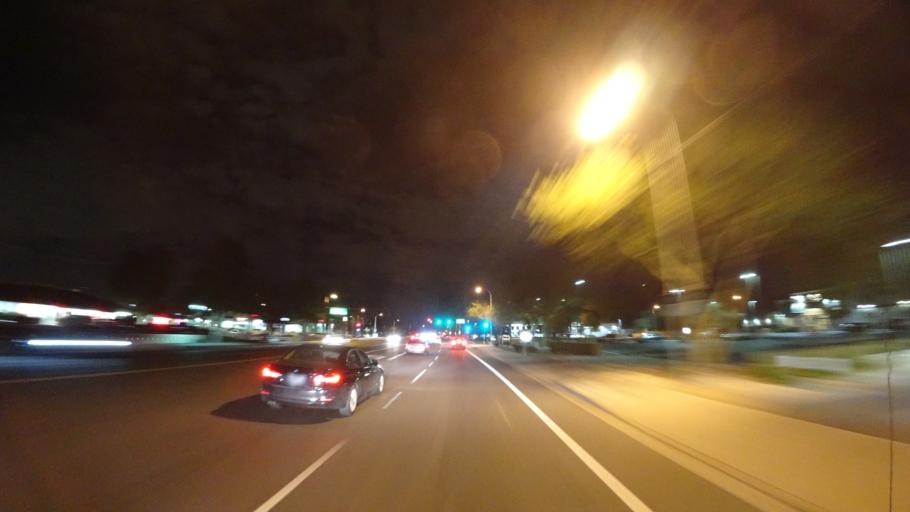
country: US
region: Arizona
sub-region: Maricopa County
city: Tempe
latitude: 33.4065
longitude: -111.9090
